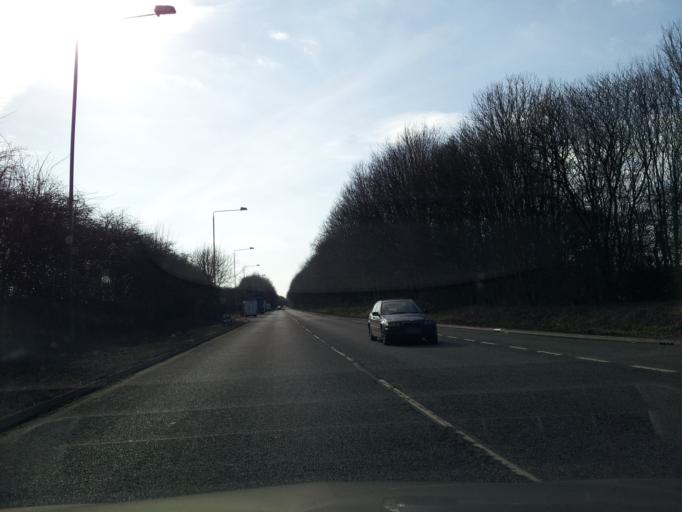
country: GB
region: England
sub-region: Nottinghamshire
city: West Bridgford
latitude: 52.9153
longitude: -1.1008
